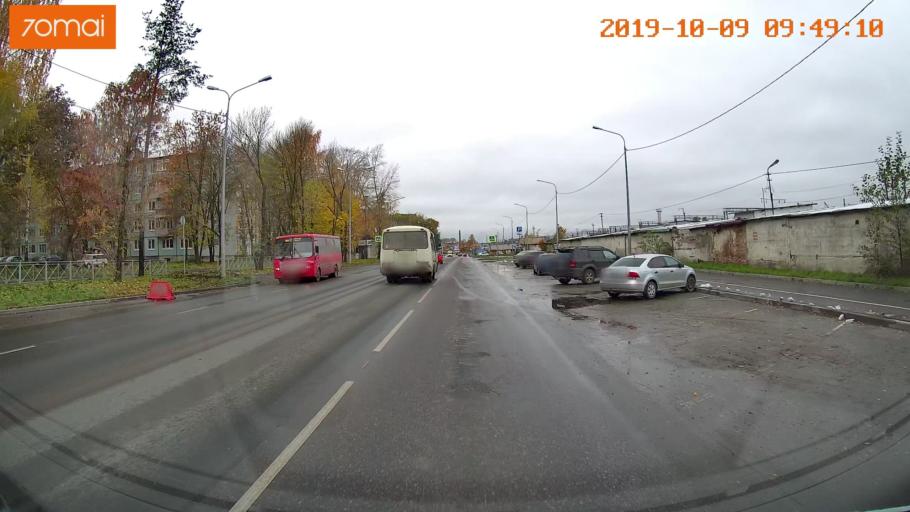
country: RU
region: Vologda
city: Vologda
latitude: 59.1975
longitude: 39.9168
